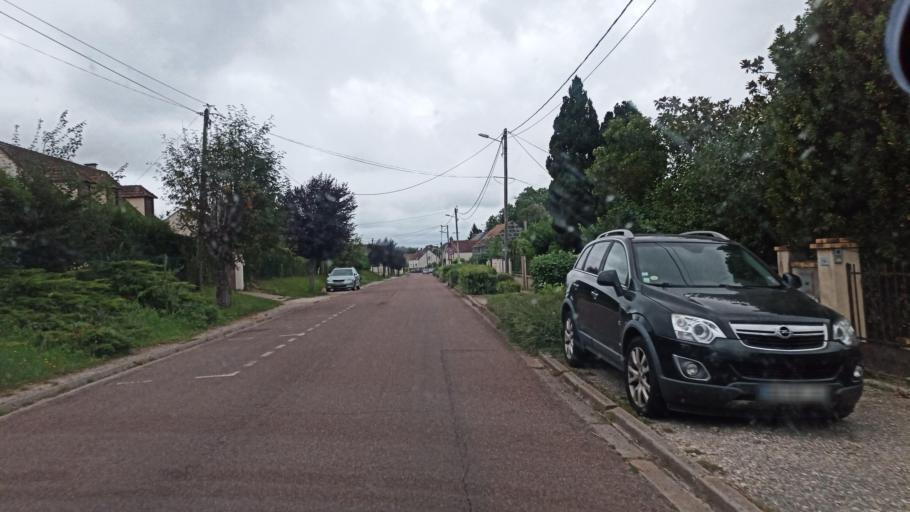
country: FR
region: Ile-de-France
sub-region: Departement de Seine-et-Marne
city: Voulx
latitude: 48.2796
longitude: 2.9752
